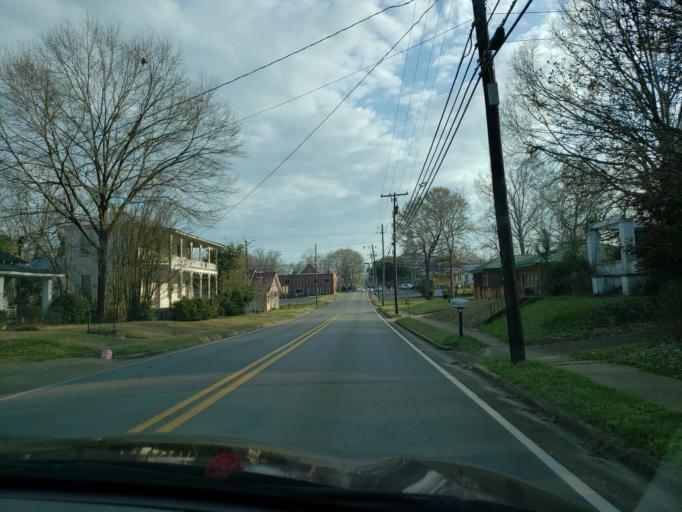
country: US
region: Alabama
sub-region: Hale County
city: Greensboro
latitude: 32.7061
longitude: -87.5922
